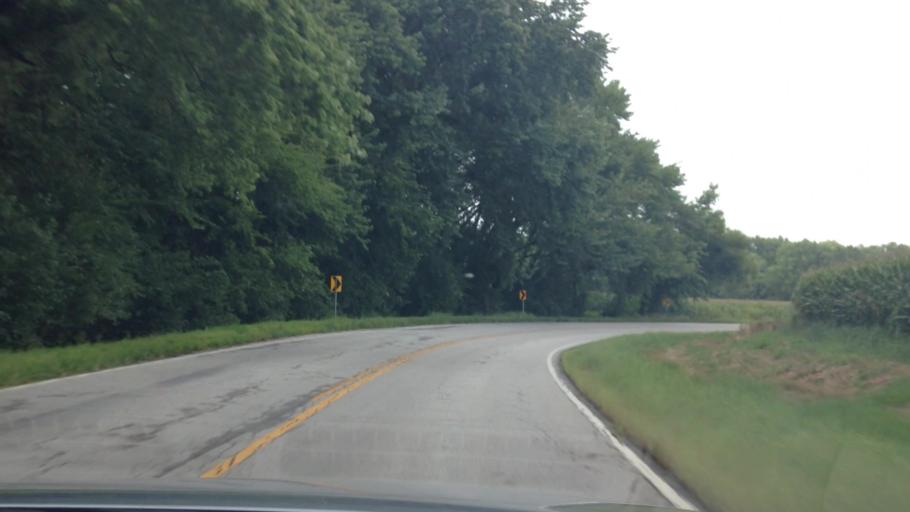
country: US
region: Missouri
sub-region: Clay County
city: Smithville
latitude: 39.4033
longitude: -94.6619
